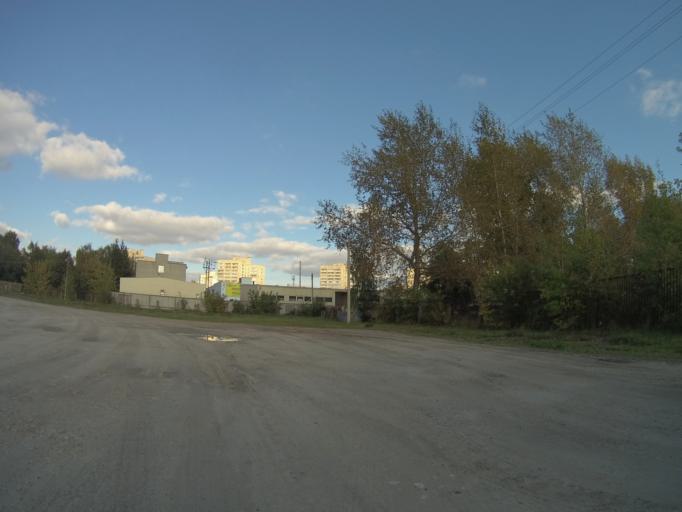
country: RU
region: Vladimir
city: Vladimir
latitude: 56.1141
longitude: 40.3390
